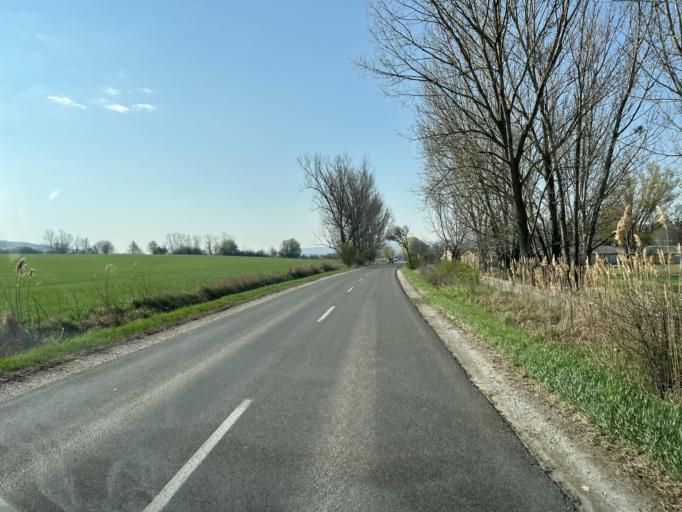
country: HU
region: Pest
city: Galgamacsa
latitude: 47.6925
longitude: 19.4024
